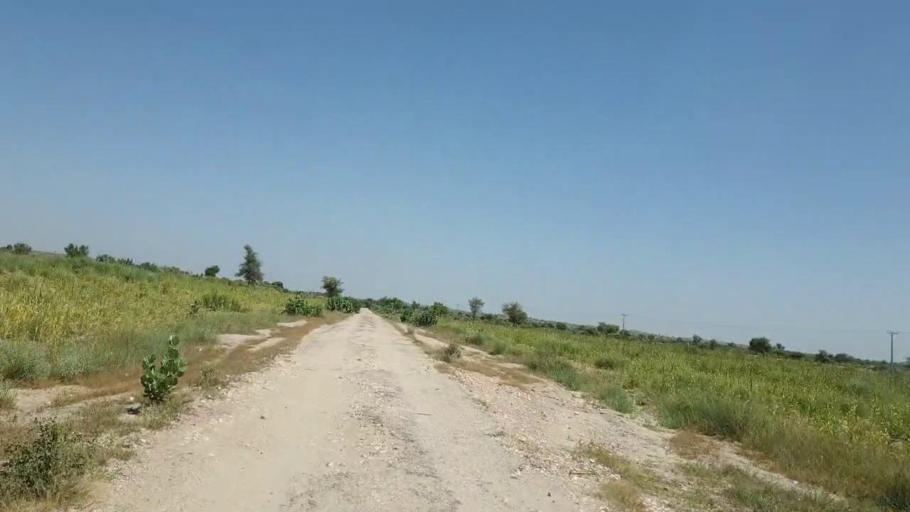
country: PK
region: Sindh
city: Islamkot
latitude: 25.1424
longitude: 70.3982
